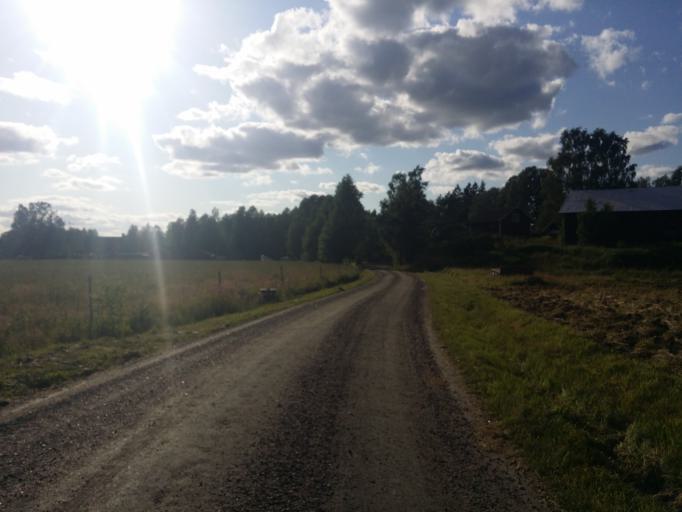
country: SE
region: OEstergoetland
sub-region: Norrkopings Kommun
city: Svartinge
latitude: 58.7190
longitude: 15.9519
